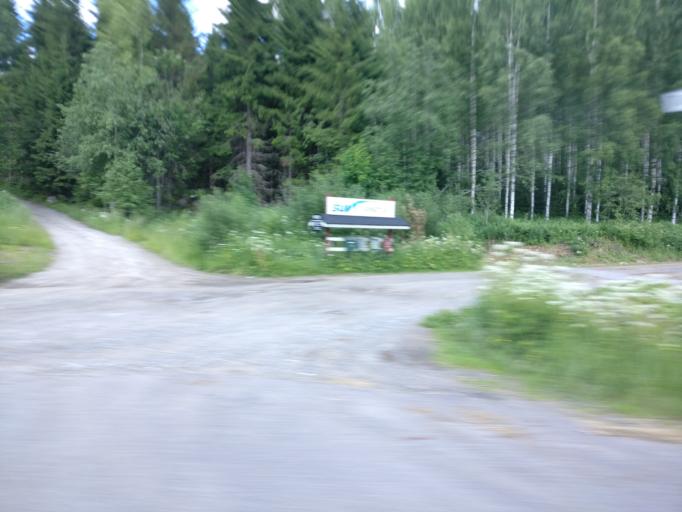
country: FI
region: Southern Savonia
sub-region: Savonlinna
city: Kerimaeki
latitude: 61.8604
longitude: 29.1527
